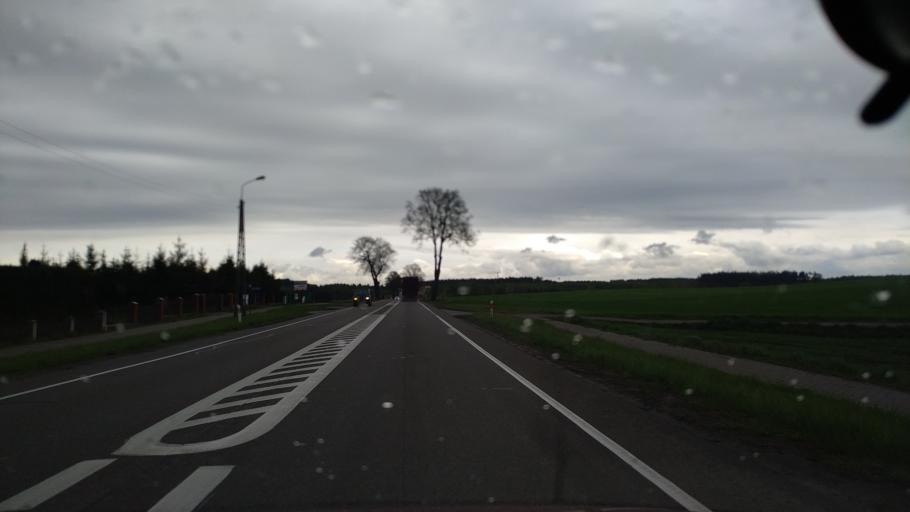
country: PL
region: Pomeranian Voivodeship
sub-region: Powiat starogardzki
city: Kaliska
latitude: 53.8888
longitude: 18.2181
